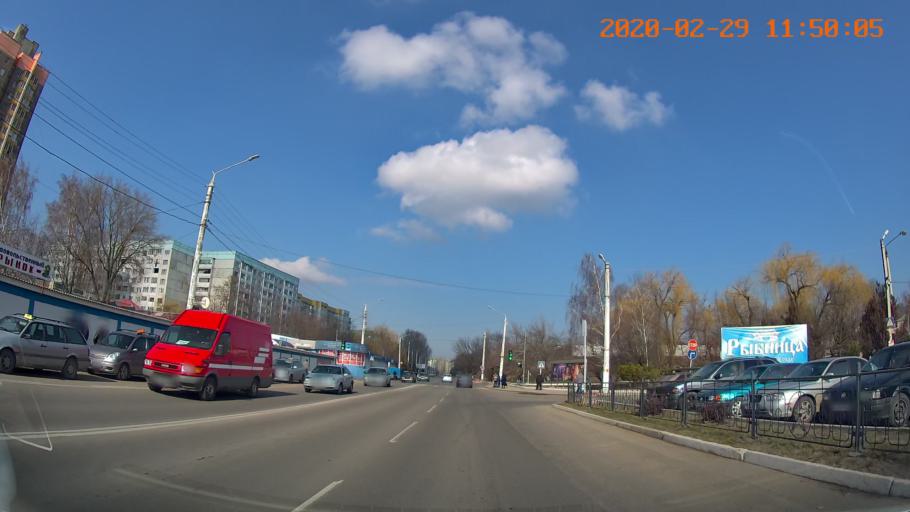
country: MD
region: Telenesti
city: Ribnita
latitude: 47.7556
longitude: 28.9915
